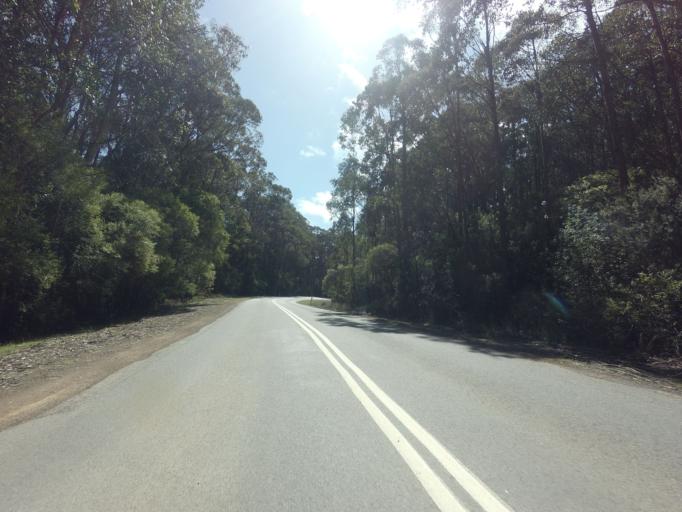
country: AU
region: Tasmania
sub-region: Derwent Valley
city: New Norfolk
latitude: -42.7298
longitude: 146.6704
